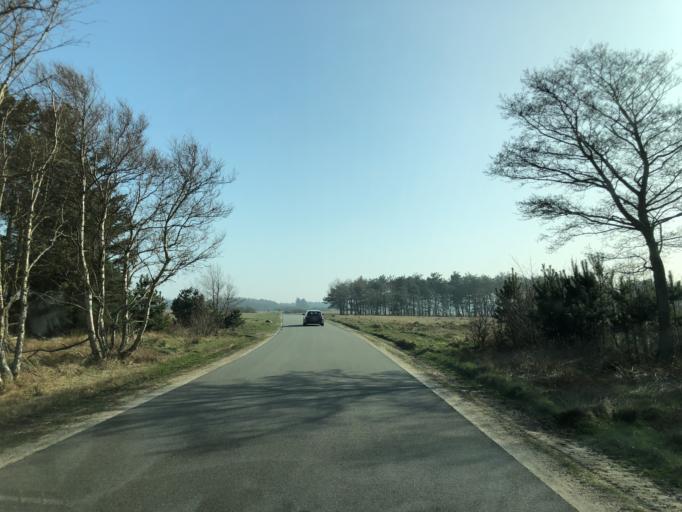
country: DK
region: South Denmark
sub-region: Varde Kommune
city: Oksbol
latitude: 55.6258
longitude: 8.1696
